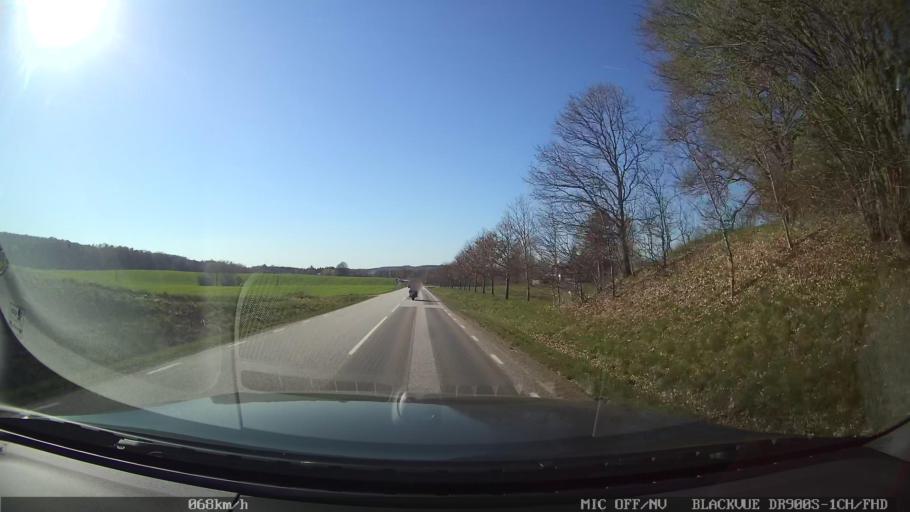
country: SE
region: Skane
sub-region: Klippans Kommun
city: Ljungbyhed
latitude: 55.9773
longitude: 13.1988
